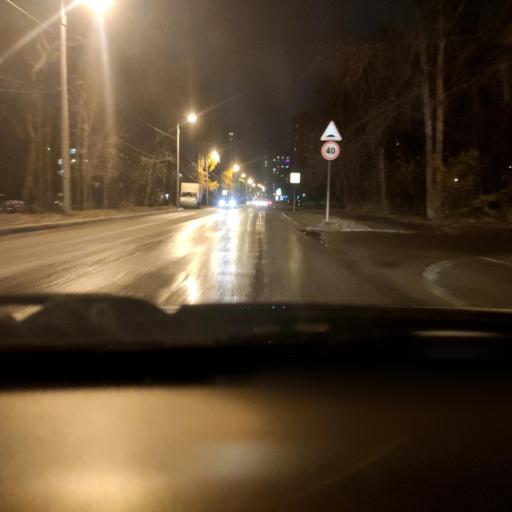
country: RU
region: Perm
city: Perm
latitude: 57.9833
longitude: 56.2910
